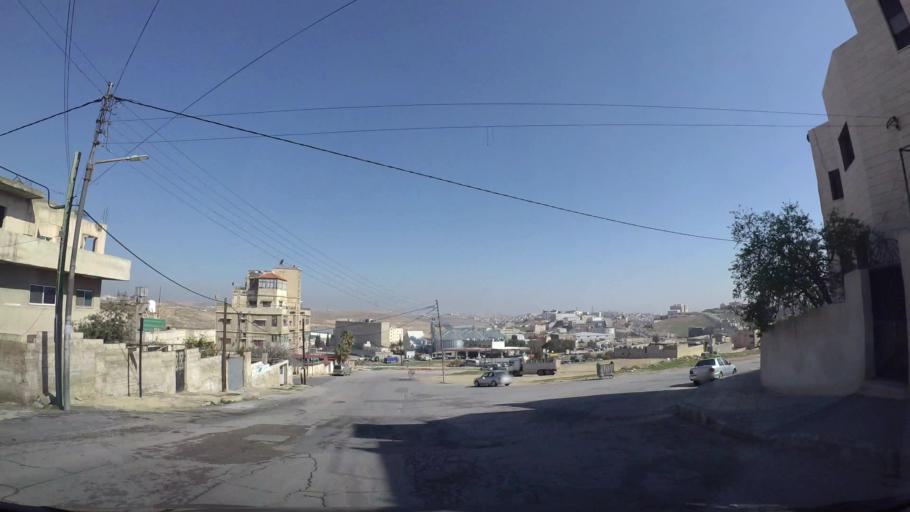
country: JO
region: Amman
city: Amman
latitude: 31.9920
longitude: 35.9890
